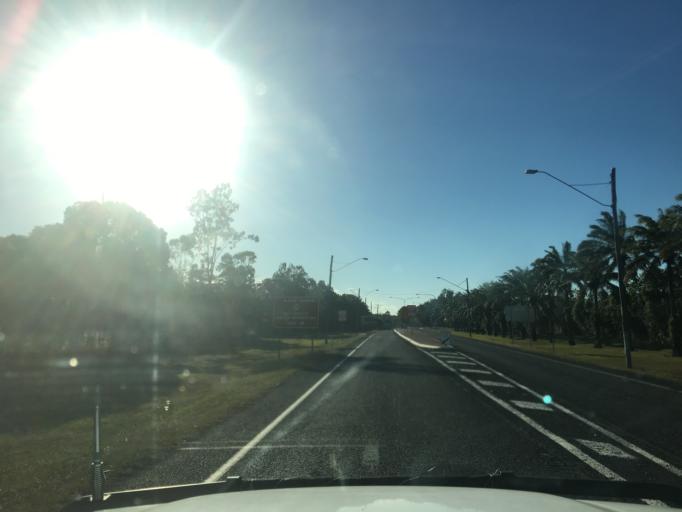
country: AU
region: Queensland
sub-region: Cairns
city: Port Douglas
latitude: -16.5302
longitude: 145.4632
